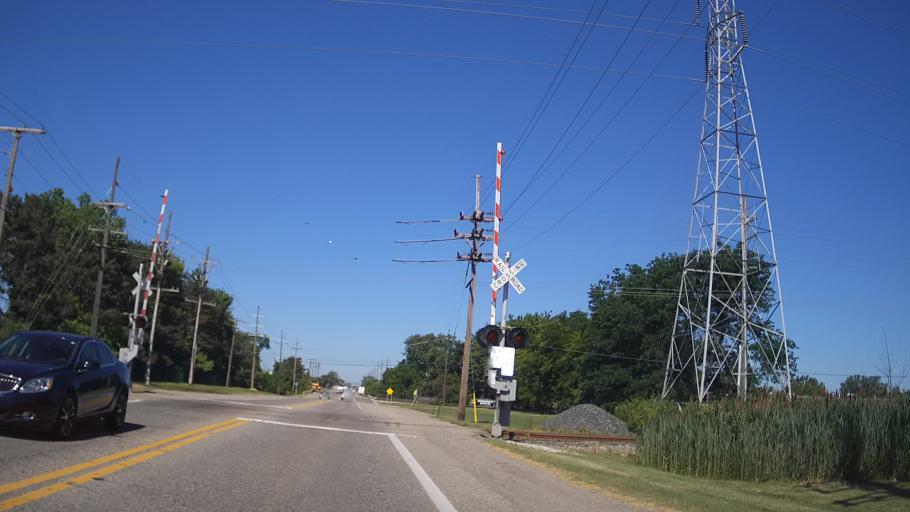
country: US
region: Michigan
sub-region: Macomb County
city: Sterling Heights
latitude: 42.5947
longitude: -83.0404
